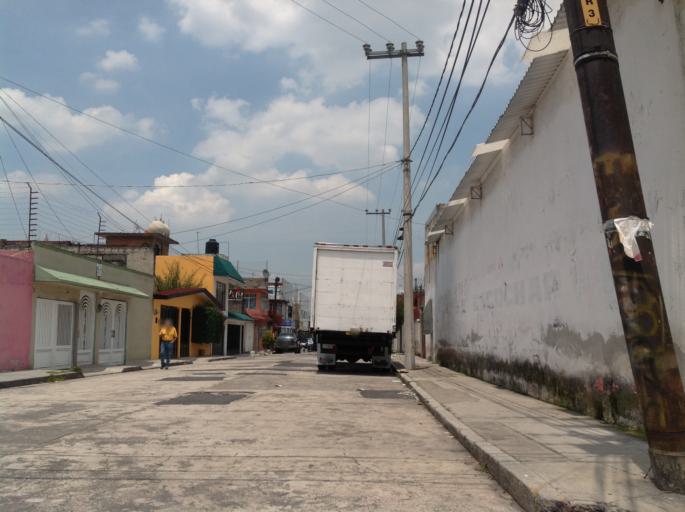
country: MX
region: Mexico
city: Ciudad Lopez Mateos
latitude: 19.5892
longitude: -99.2327
